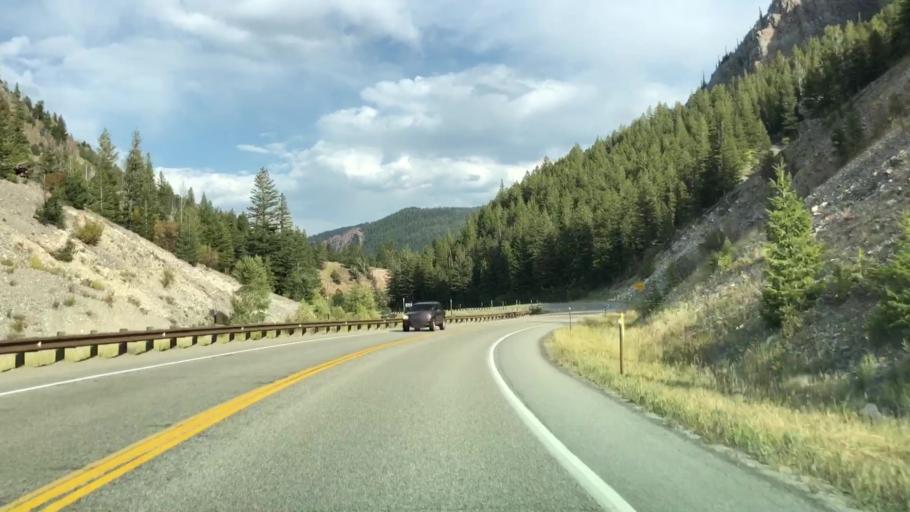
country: US
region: Wyoming
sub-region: Teton County
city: Hoback
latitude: 43.2837
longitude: -110.6241
